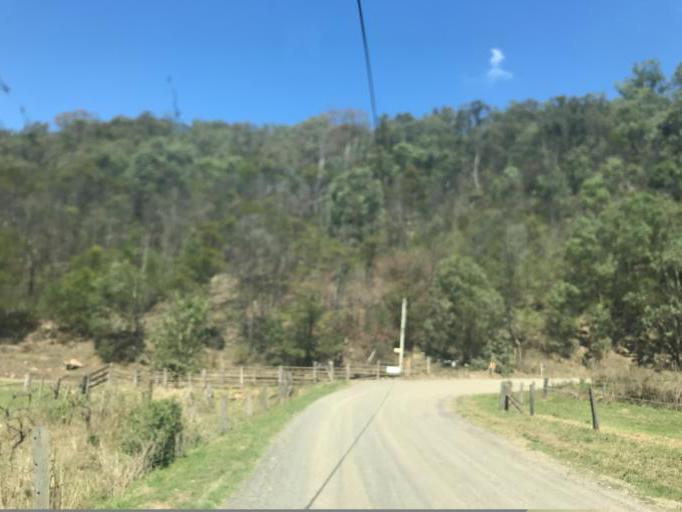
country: AU
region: New South Wales
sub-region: Hornsby Shire
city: Glenorie
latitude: -33.2750
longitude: 150.9693
